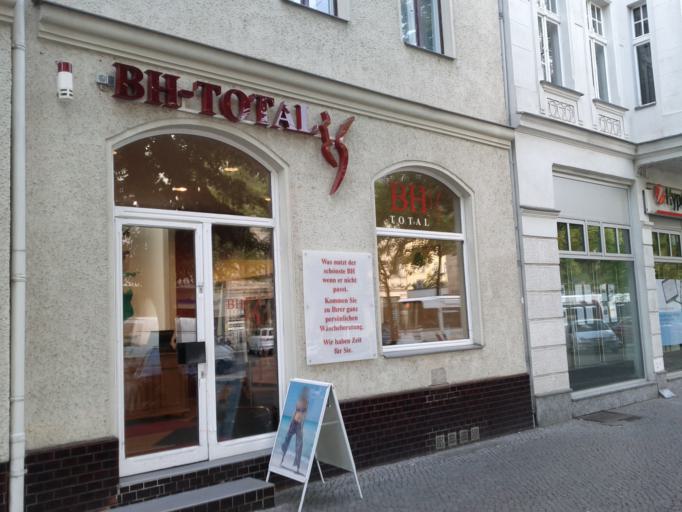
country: DE
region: Berlin
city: Friedrichshagen
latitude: 52.4545
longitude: 13.6250
